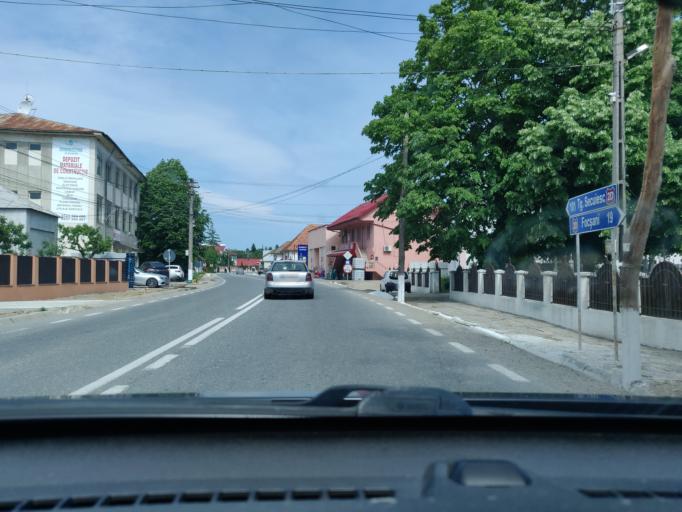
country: RO
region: Vrancea
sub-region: Comuna Bolotesti
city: Bolotesti
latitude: 45.8396
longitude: 27.0735
